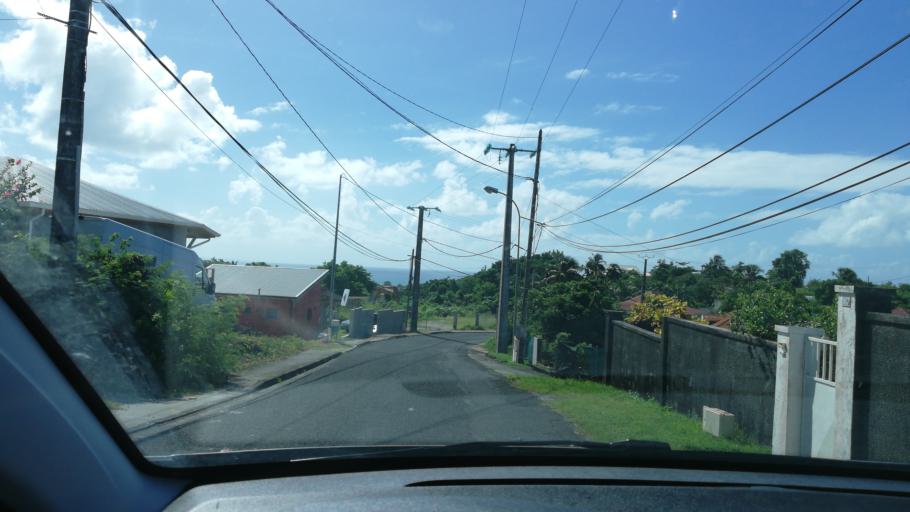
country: GP
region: Guadeloupe
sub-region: Guadeloupe
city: Le Gosier
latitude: 16.2141
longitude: -61.4547
